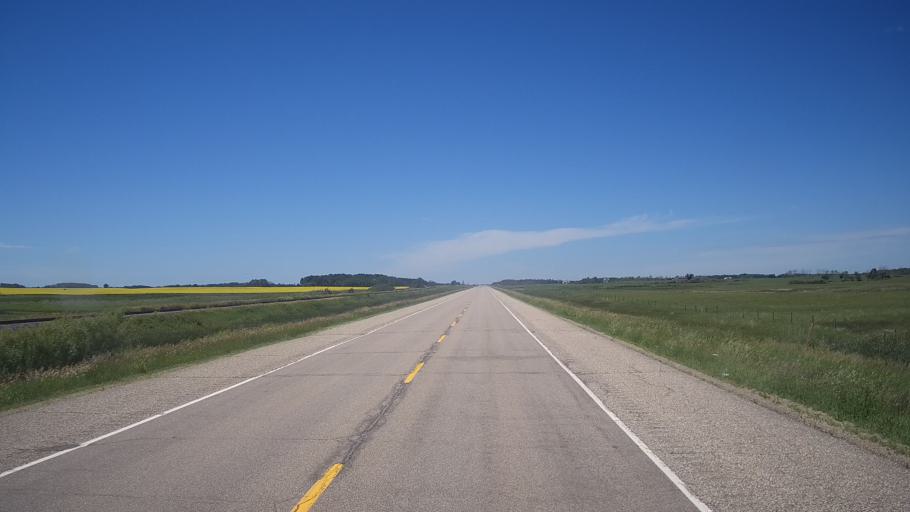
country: CA
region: Manitoba
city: Rivers
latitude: 50.4216
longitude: -100.4947
